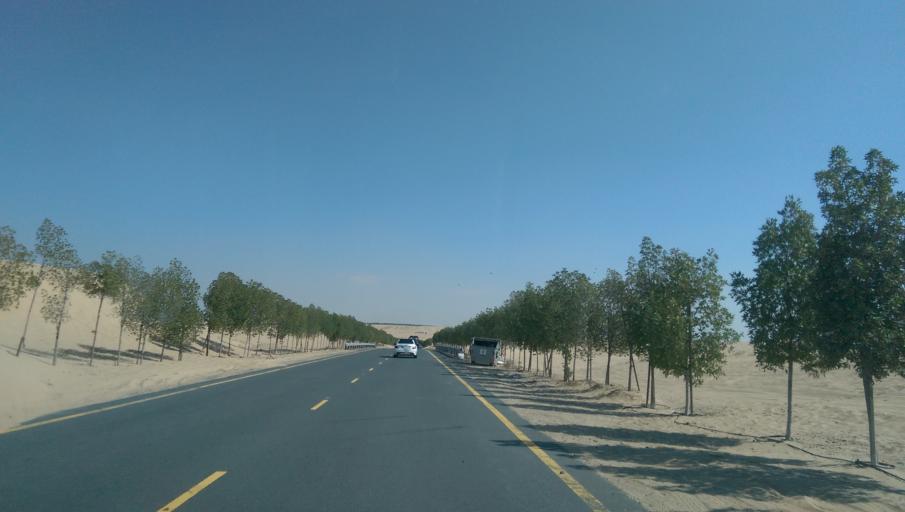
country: AE
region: Dubai
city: Dubai
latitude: 24.9833
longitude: 55.3436
